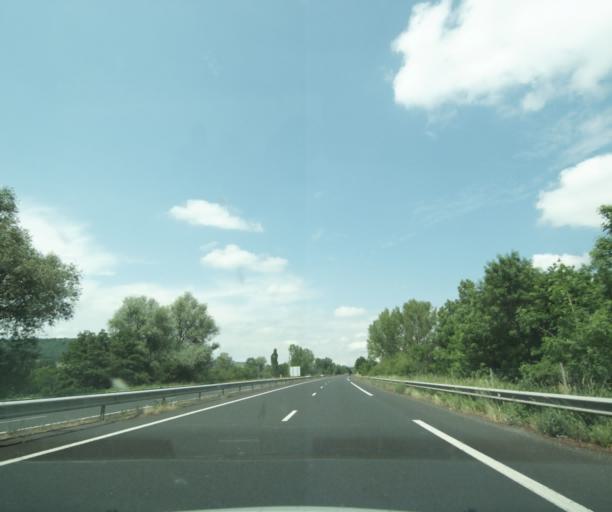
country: FR
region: Auvergne
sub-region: Departement de la Haute-Loire
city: Lempdes-sur-Allagnon
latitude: 45.3898
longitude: 3.2748
